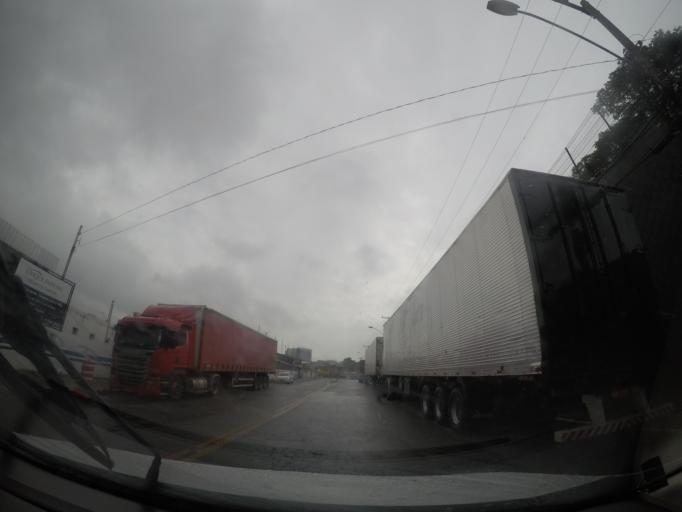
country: BR
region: Sao Paulo
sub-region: Guarulhos
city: Guarulhos
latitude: -23.4395
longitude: -46.5065
